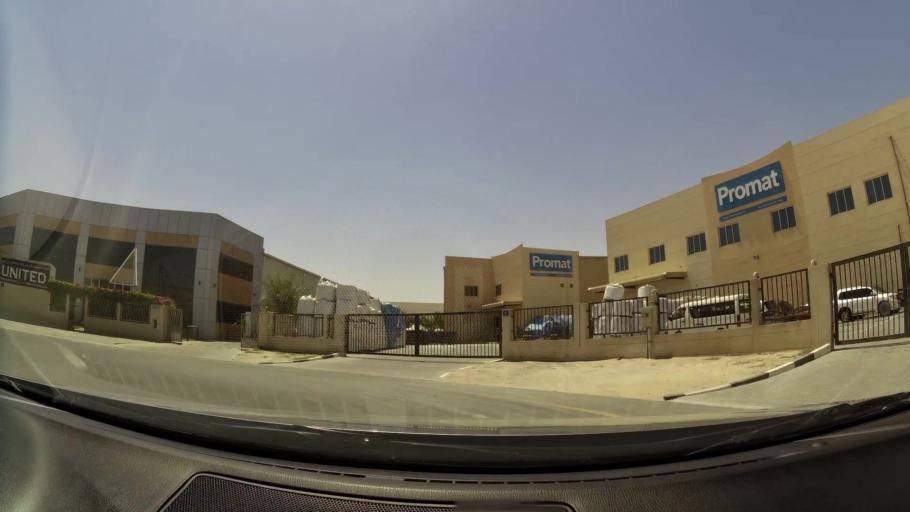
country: AE
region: Dubai
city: Dubai
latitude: 24.9792
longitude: 55.1918
